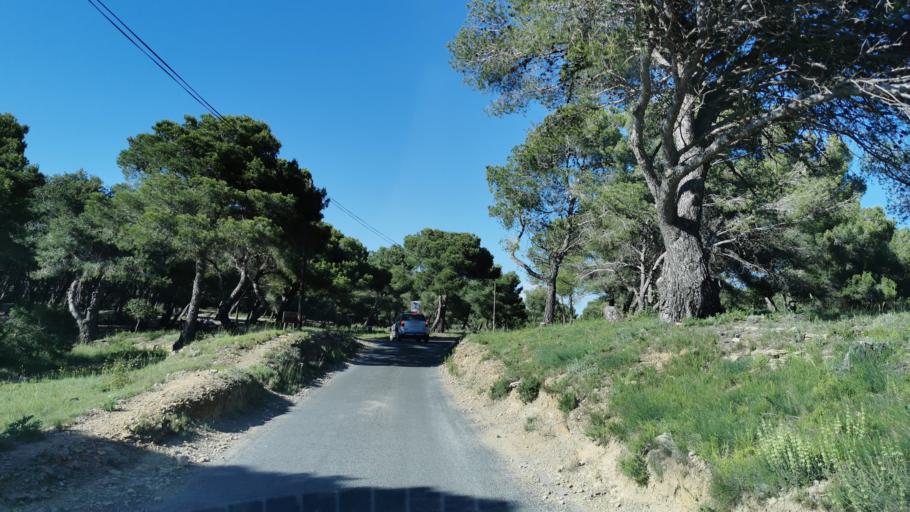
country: FR
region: Languedoc-Roussillon
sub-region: Departement de l'Aude
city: Gruissan
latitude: 43.1298
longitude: 3.0998
